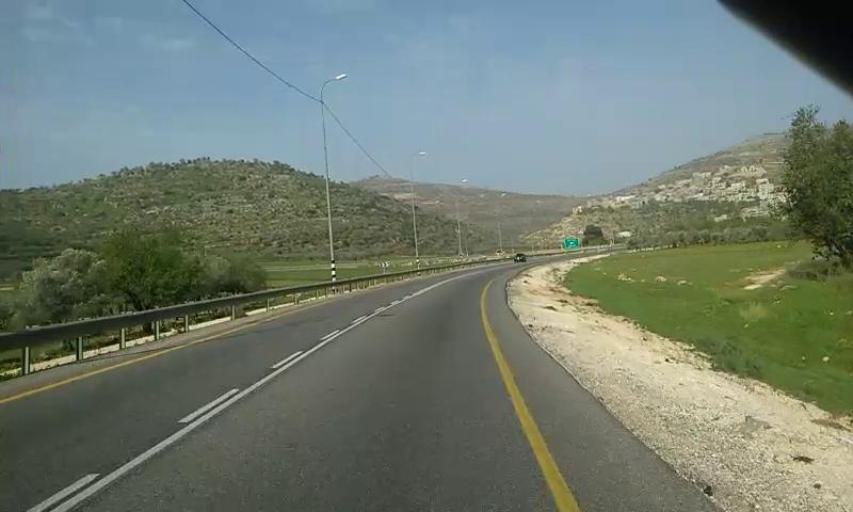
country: PS
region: West Bank
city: Al Lubban ash Sharqiyah
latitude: 32.0670
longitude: 35.2464
